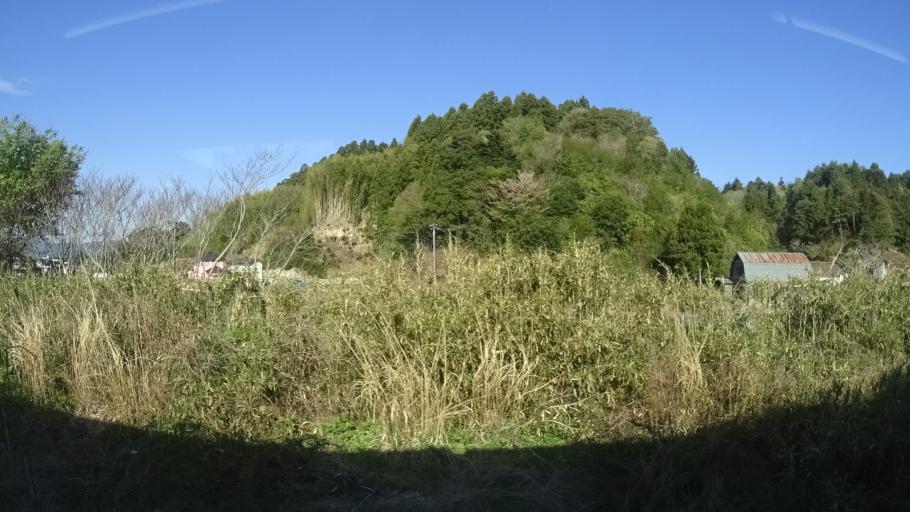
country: JP
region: Fukushima
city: Namie
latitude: 37.5710
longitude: 140.9975
